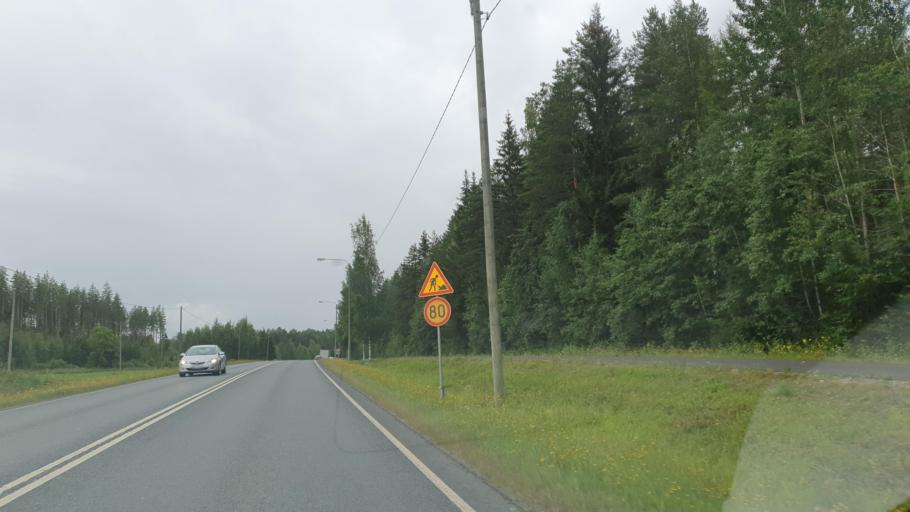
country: FI
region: Northern Savo
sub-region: Kuopio
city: Siilinjaervi
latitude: 63.1320
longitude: 27.6240
